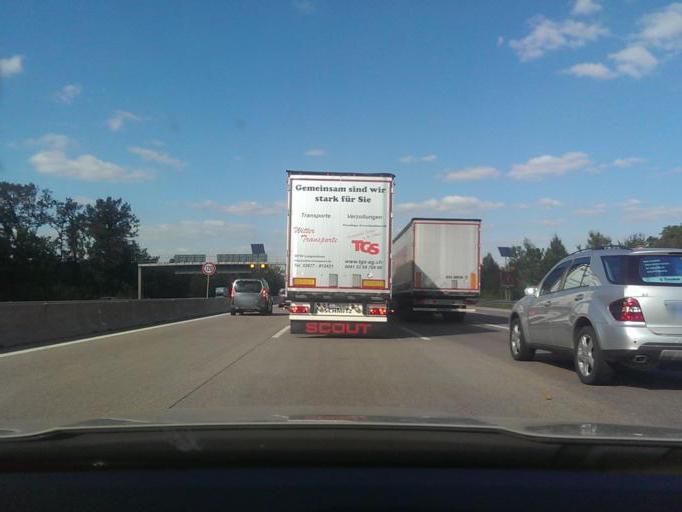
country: DE
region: Baden-Wuerttemberg
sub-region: Karlsruhe Region
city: Karlsruhe
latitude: 48.9794
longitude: 8.4371
